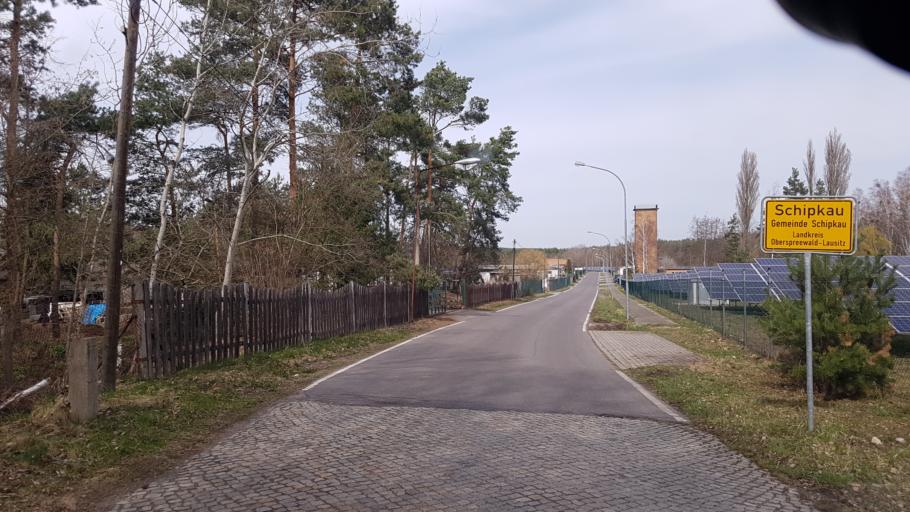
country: DE
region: Brandenburg
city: Schipkau
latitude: 51.5091
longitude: 13.8906
